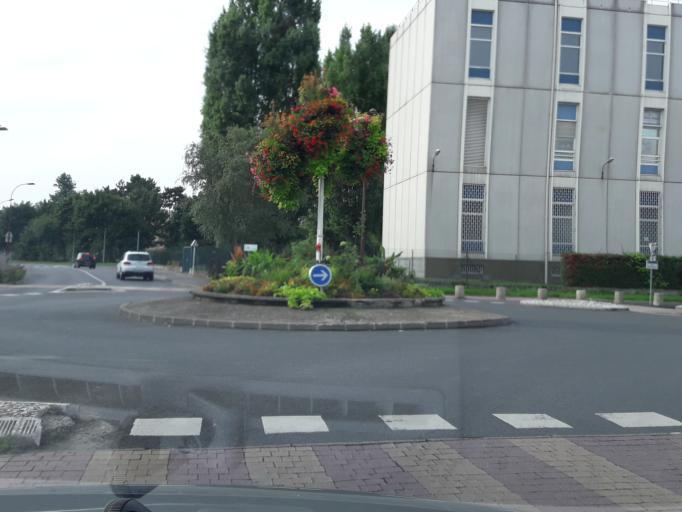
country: FR
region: Ile-de-France
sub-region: Departement de l'Essonne
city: Fleury-Merogis
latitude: 48.6385
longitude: 2.3454
